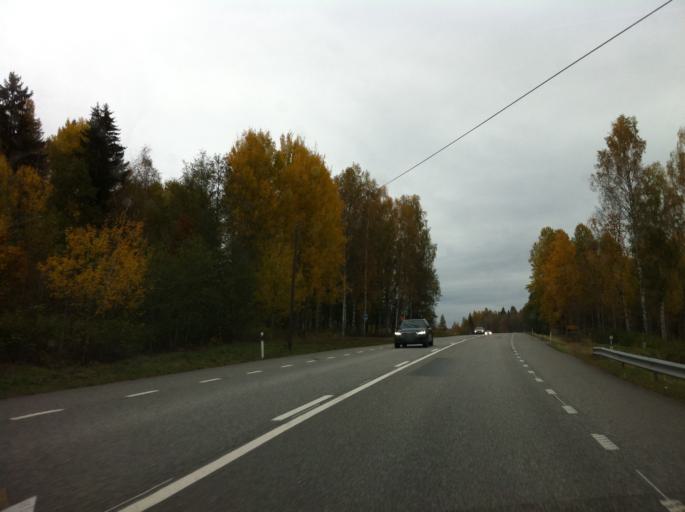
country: SE
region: OErebro
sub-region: Lindesbergs Kommun
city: Stora
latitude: 59.7845
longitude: 15.1518
